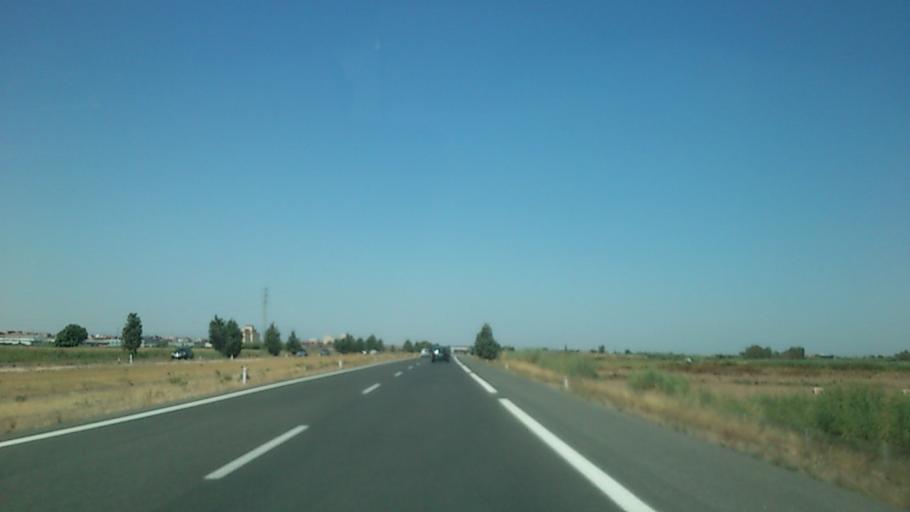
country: ES
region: Aragon
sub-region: Provincia de Zaragoza
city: Utebo
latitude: 41.7203
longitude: -1.0019
